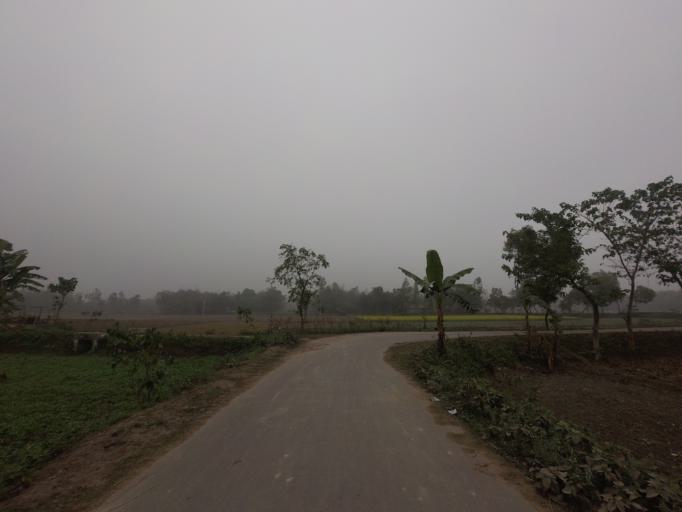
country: BD
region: Rajshahi
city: Saidpur
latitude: 26.0427
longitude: 88.8732
